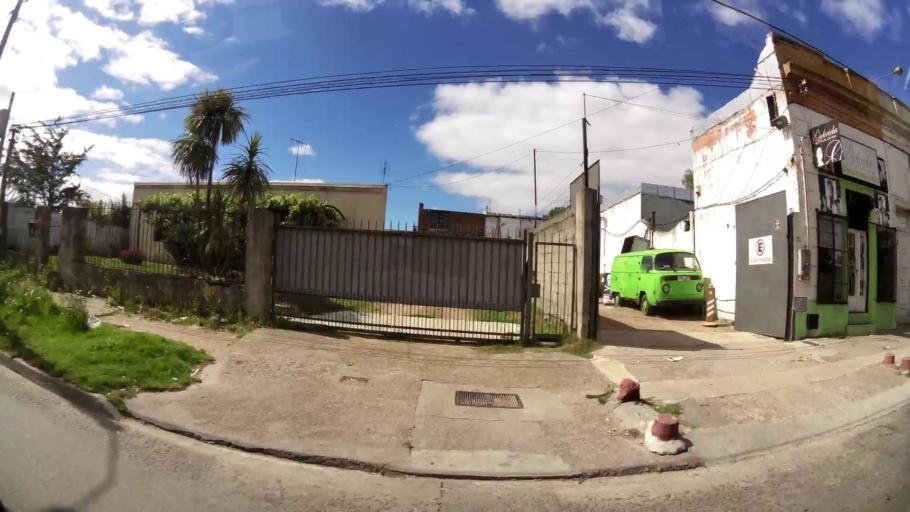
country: UY
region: Canelones
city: Paso de Carrasco
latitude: -34.8711
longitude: -56.1153
